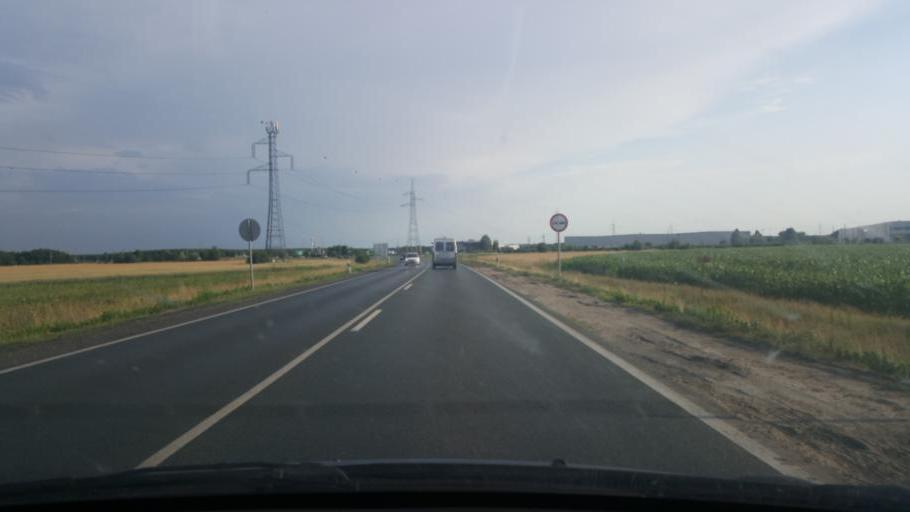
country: HU
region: Pest
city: Ullo
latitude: 47.3800
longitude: 19.3641
